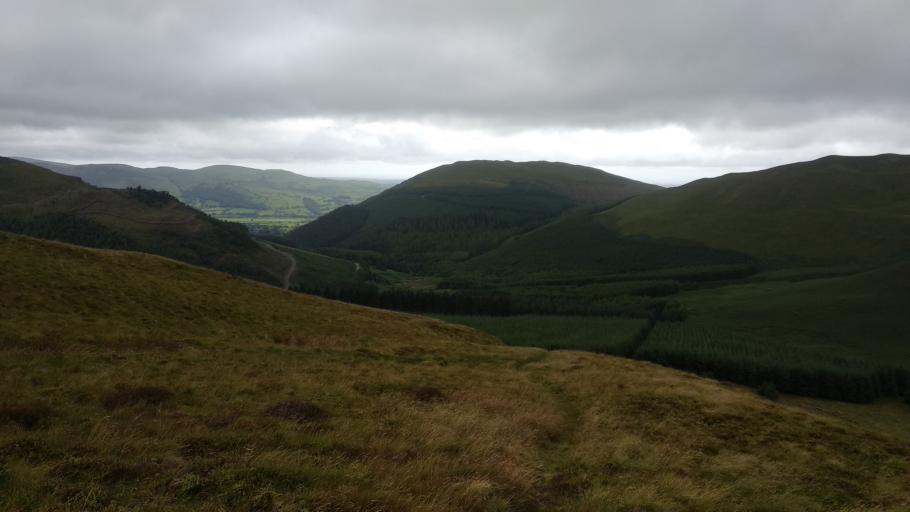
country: GB
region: England
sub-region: Cumbria
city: Keswick
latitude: 54.6257
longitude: -3.2421
